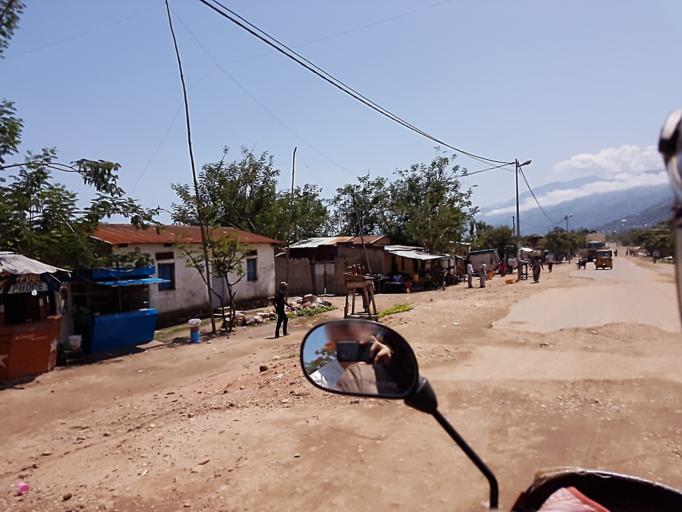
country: CD
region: South Kivu
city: Uvira
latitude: -3.3569
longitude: 29.1535
